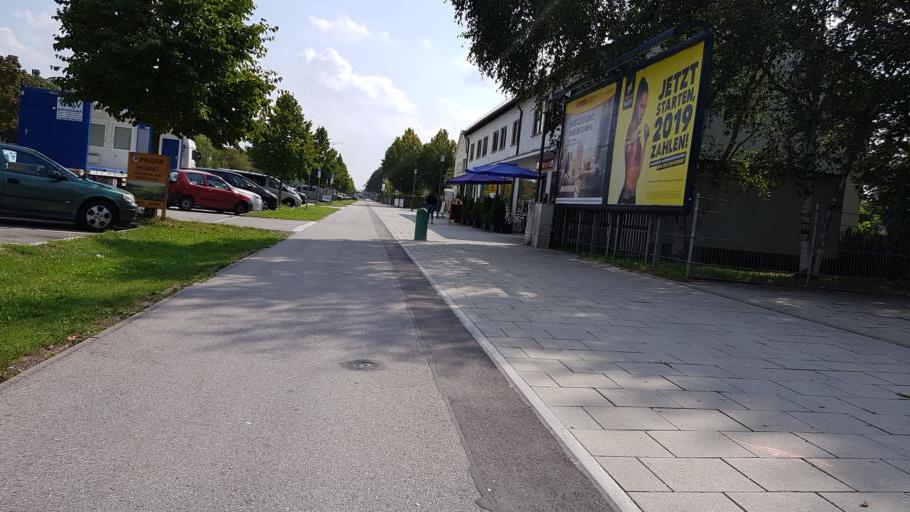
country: DE
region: Bavaria
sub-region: Upper Bavaria
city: Oberschleissheim
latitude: 48.2040
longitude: 11.5636
